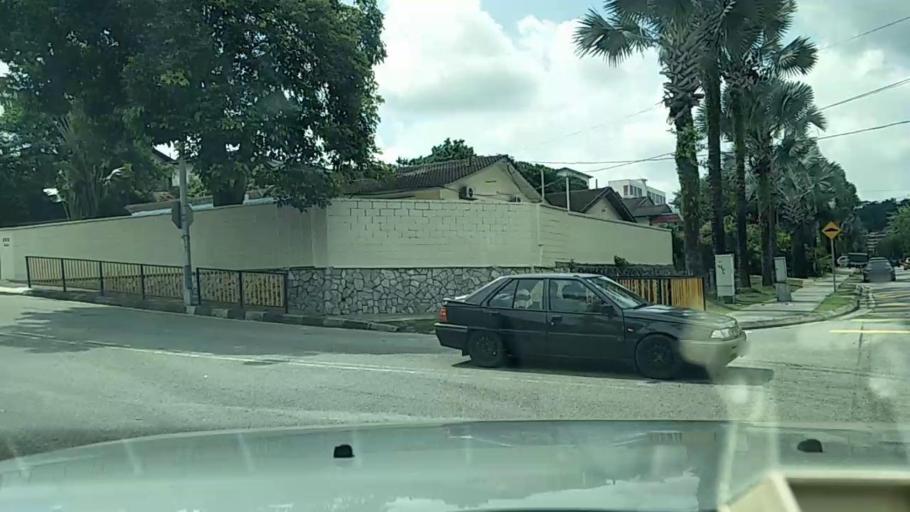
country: MY
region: Kuala Lumpur
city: Kuala Lumpur
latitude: 3.1326
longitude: 101.6733
